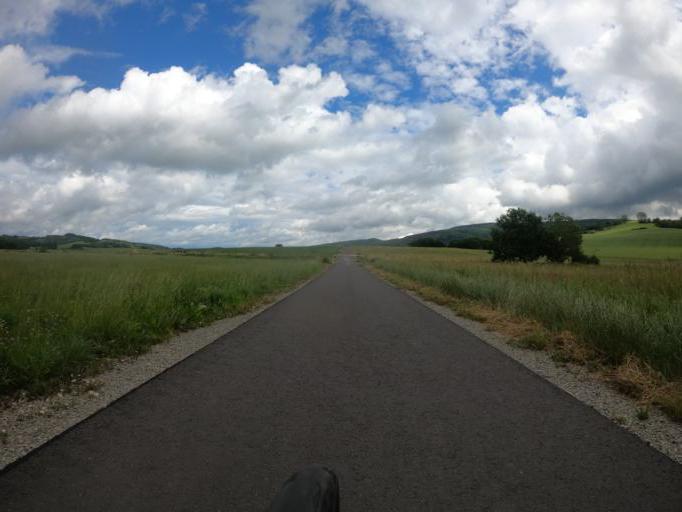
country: DE
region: Hesse
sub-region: Regierungsbezirk Kassel
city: Grossalmerode
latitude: 51.2189
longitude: 9.8006
